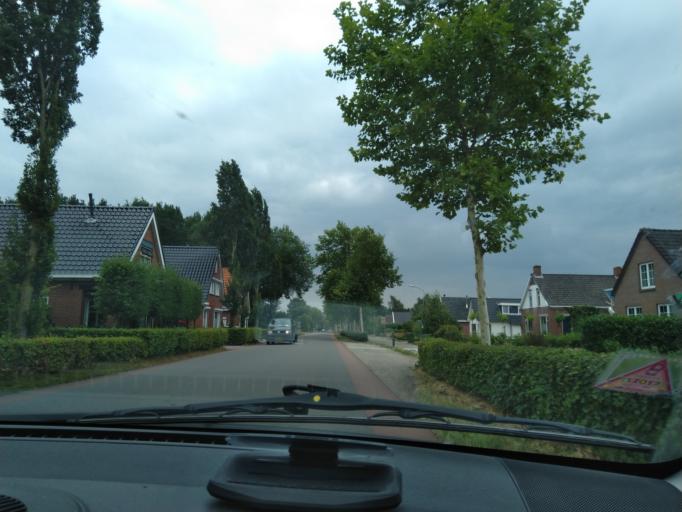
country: NL
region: Groningen
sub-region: Gemeente Vlagtwedde
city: Vlagtwedde
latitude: 53.0943
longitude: 7.1589
